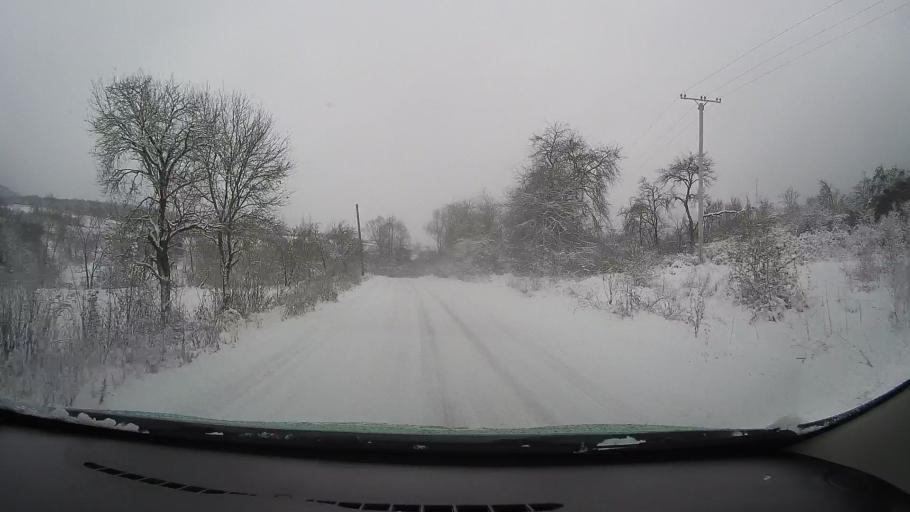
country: RO
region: Hunedoara
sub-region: Comuna Carjiti
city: Carjiti
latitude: 45.8354
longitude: 22.8392
